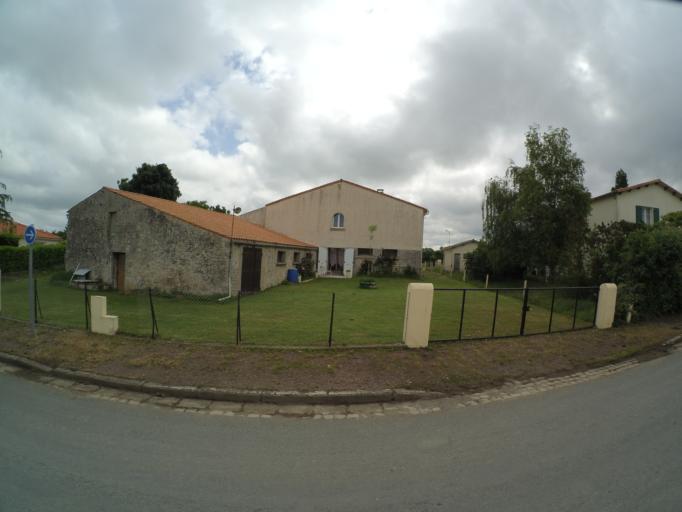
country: FR
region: Poitou-Charentes
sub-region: Departement de la Charente-Maritime
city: Yves
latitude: 46.0195
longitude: -1.0478
